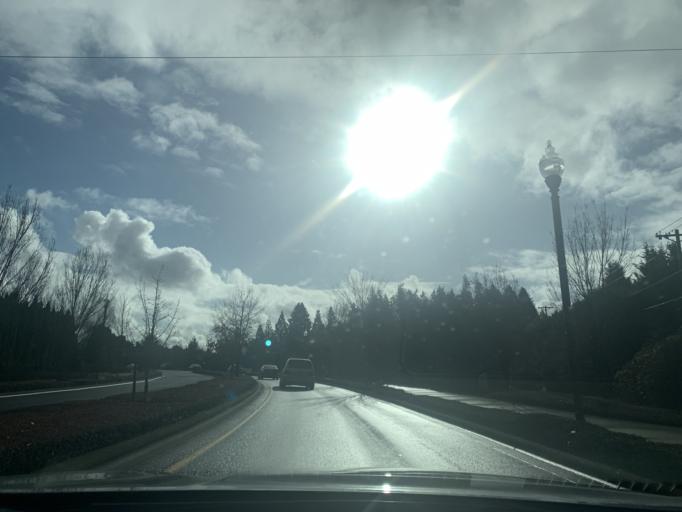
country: US
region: Oregon
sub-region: Washington County
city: Sherwood
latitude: 45.3729
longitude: -122.8567
